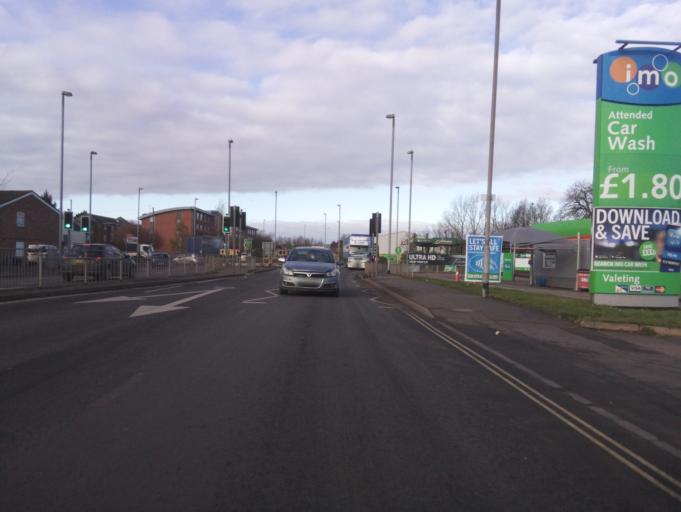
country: GB
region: England
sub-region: Staffordshire
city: Burton upon Trent
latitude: 52.7976
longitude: -1.6350
